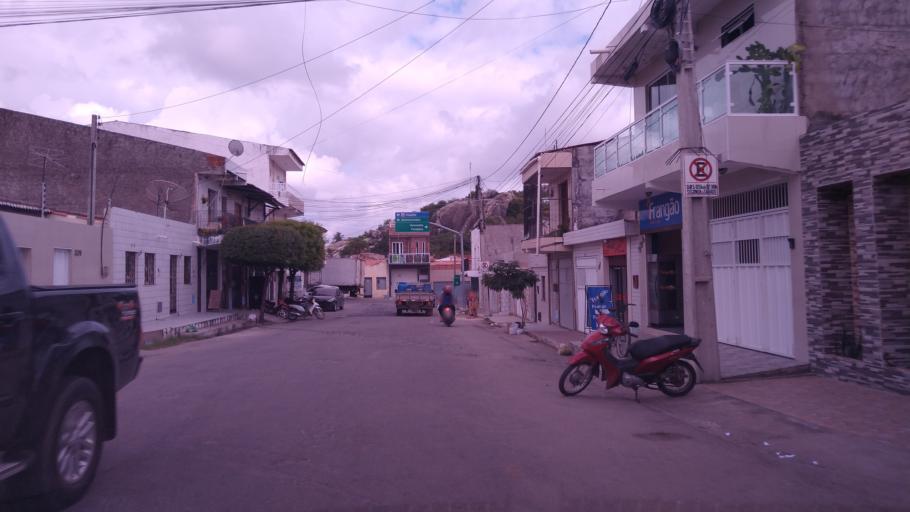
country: BR
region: Ceara
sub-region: Quixada
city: Quixada
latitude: -4.9672
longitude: -39.0187
